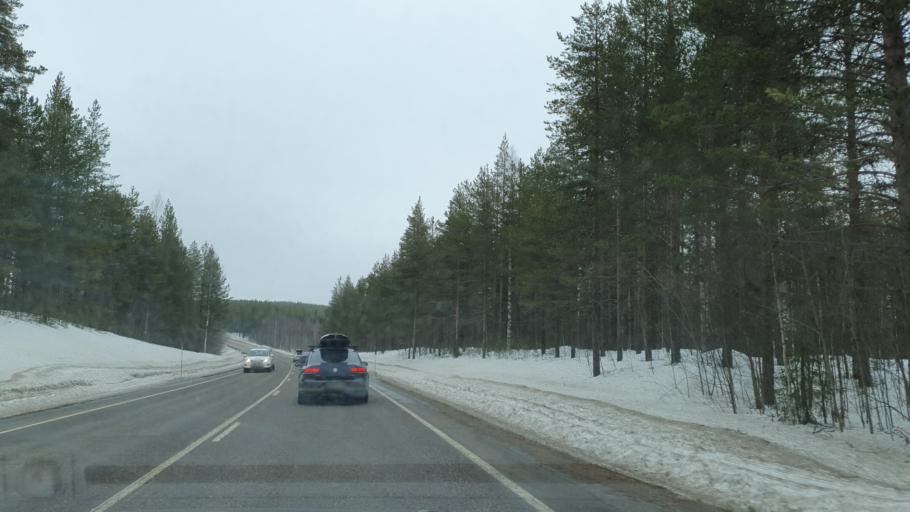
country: FI
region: Lapland
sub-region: Torniolaakso
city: Pello
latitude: 66.8493
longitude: 24.0417
